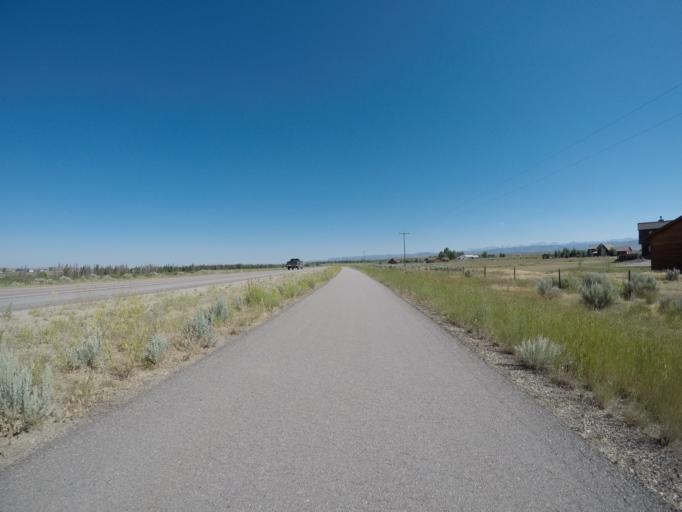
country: US
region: Wyoming
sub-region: Sublette County
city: Pinedale
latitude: 42.8419
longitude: -109.8467
